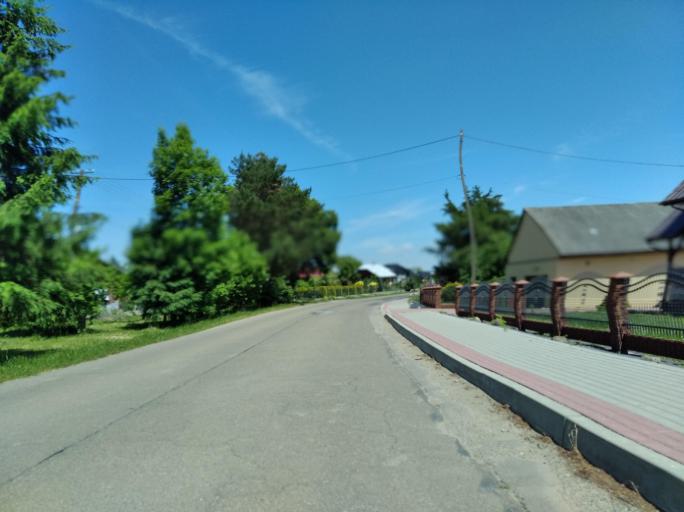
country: PL
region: Subcarpathian Voivodeship
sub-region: Powiat jasielski
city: Tarnowiec
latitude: 49.7176
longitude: 21.5559
